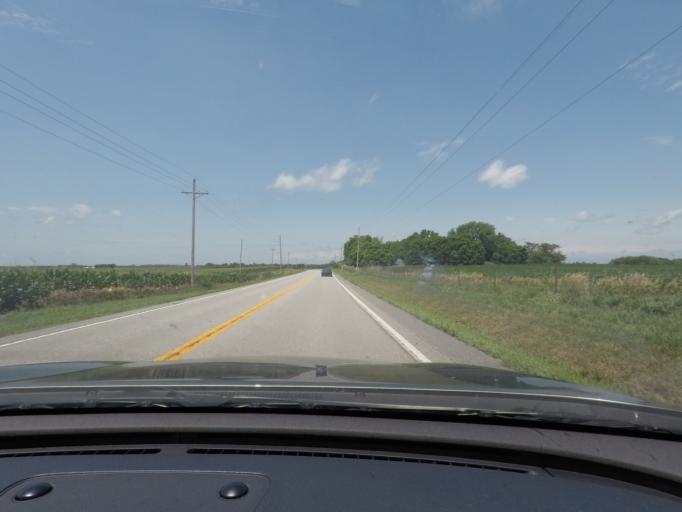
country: US
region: Missouri
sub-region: Saline County
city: Marshall
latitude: 39.1595
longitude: -93.2684
